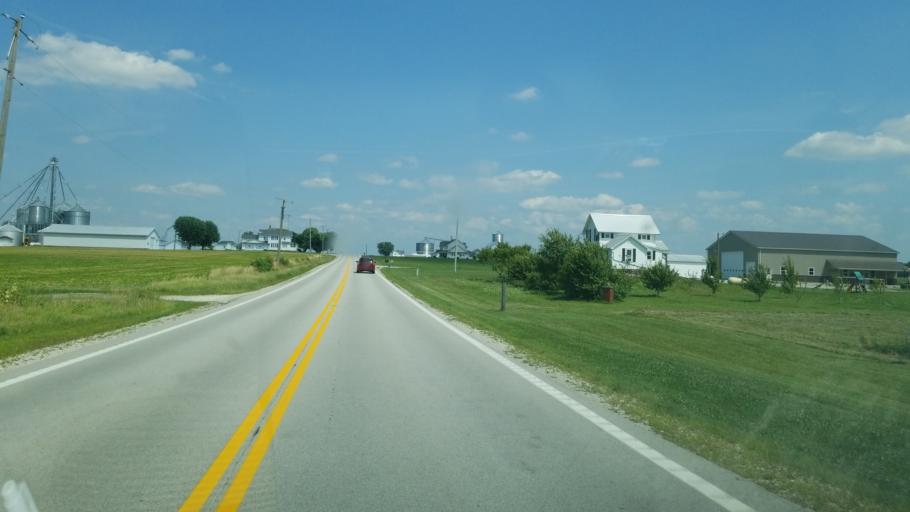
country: US
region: Ohio
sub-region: Sandusky County
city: Mount Carmel
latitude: 41.1246
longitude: -82.9166
